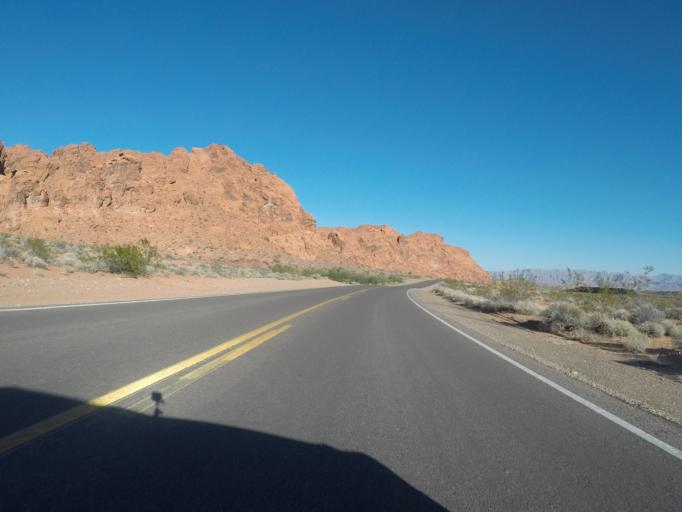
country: US
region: Nevada
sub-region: Clark County
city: Moapa Valley
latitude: 36.4275
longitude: -114.4985
